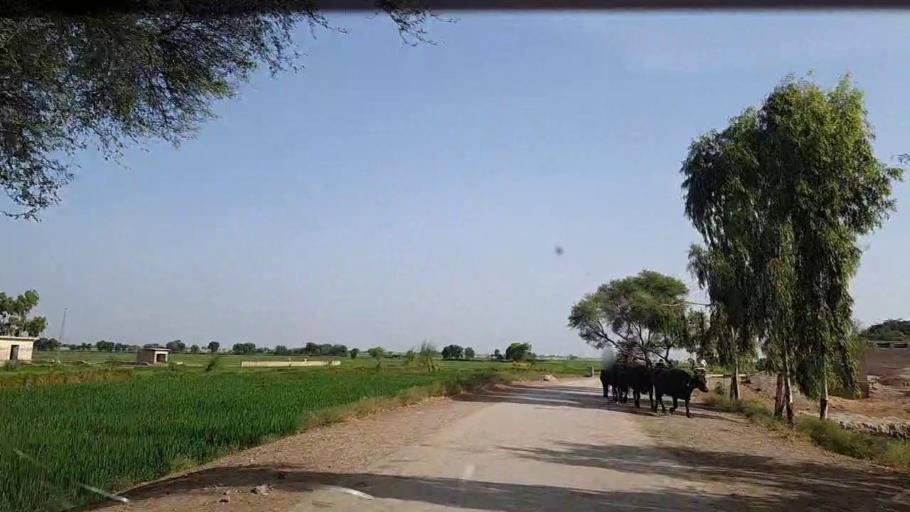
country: PK
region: Sindh
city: Khairpur Nathan Shah
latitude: 27.0054
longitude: 67.6710
